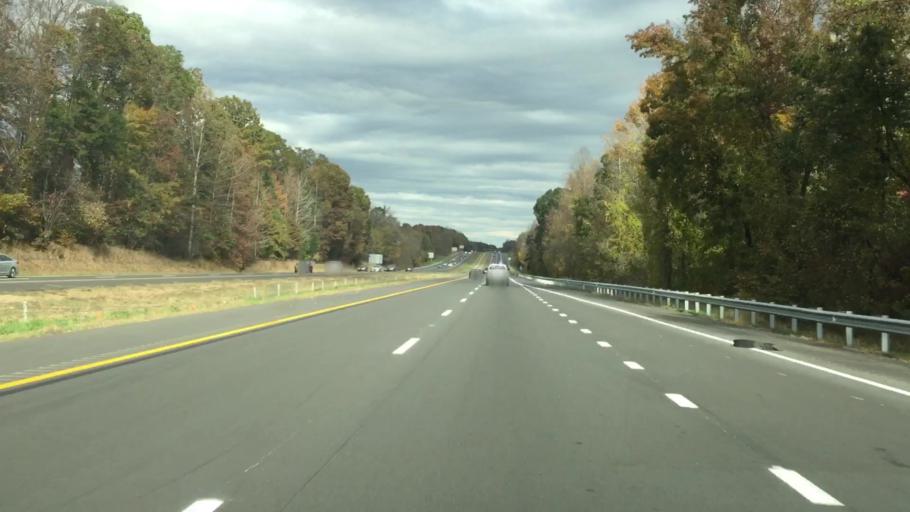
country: US
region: North Carolina
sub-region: Davie County
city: Mocksville
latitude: 35.9263
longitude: -80.5843
